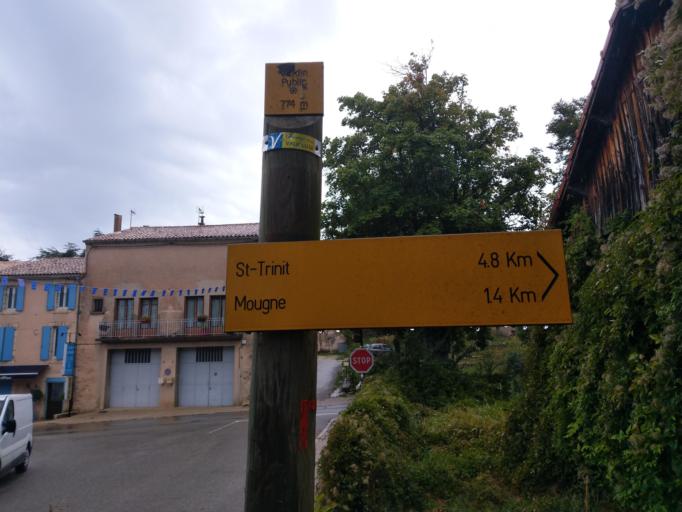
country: FR
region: Provence-Alpes-Cote d'Azur
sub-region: Departement du Vaucluse
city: Sault
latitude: 44.0928
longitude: 5.4116
